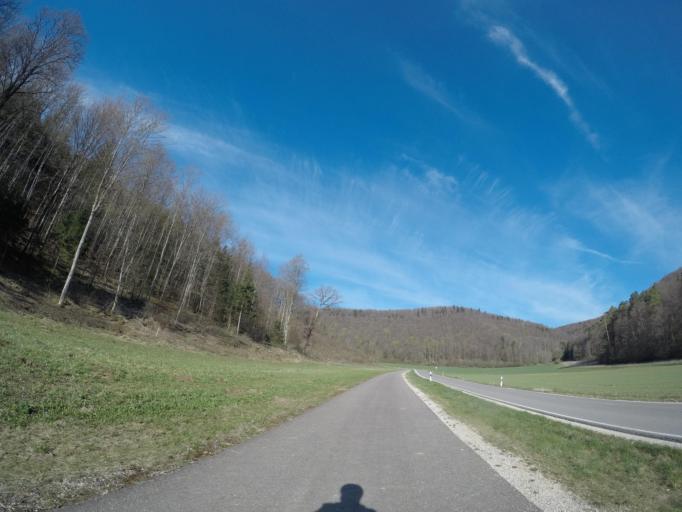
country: DE
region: Baden-Wuerttemberg
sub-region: Tuebingen Region
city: Allmendingen
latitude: 48.3474
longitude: 9.7062
